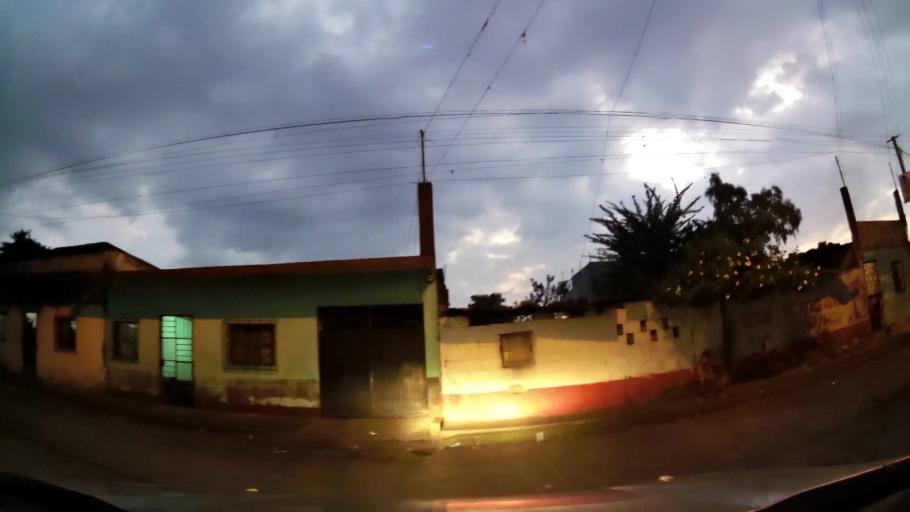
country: GT
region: Escuintla
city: Santa Lucia Cotzumalguapa
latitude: 14.3396
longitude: -91.0297
